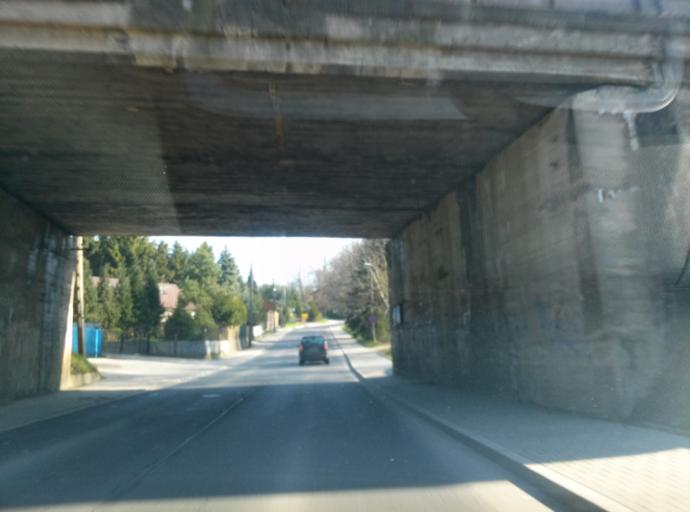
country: PL
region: Lesser Poland Voivodeship
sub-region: Powiat krakowski
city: Michalowice
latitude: 50.0942
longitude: 20.0356
